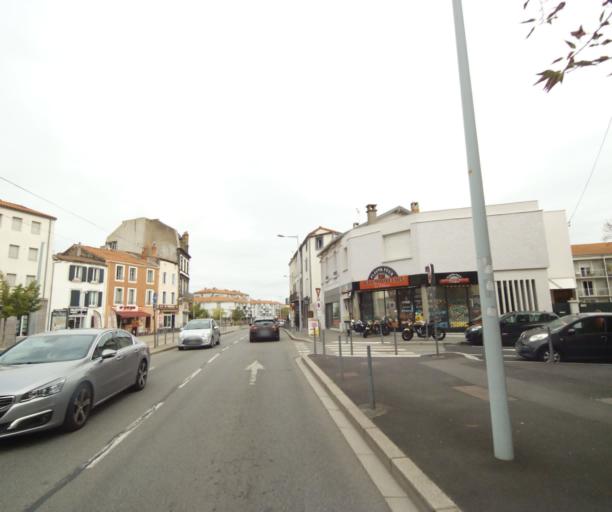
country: FR
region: Auvergne
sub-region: Departement du Puy-de-Dome
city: Clermont-Ferrand
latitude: 45.7906
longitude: 3.1124
